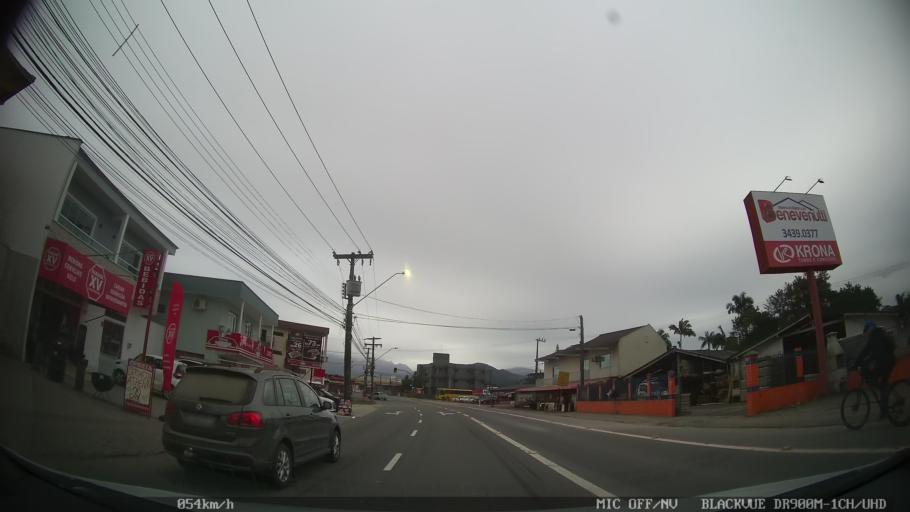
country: BR
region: Santa Catarina
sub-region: Joinville
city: Joinville
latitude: -26.2875
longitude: -48.8978
